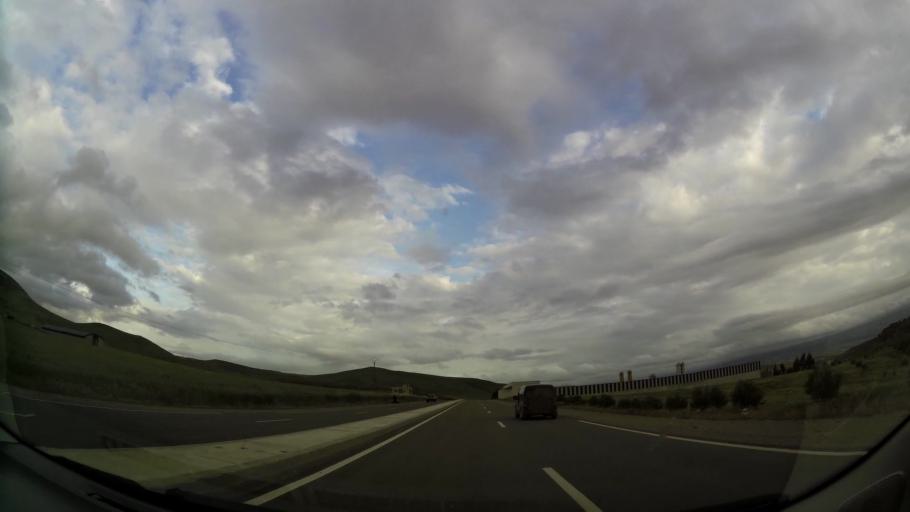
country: MA
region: Taza-Al Hoceima-Taounate
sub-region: Taza
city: Taza
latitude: 34.2822
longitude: -3.9588
